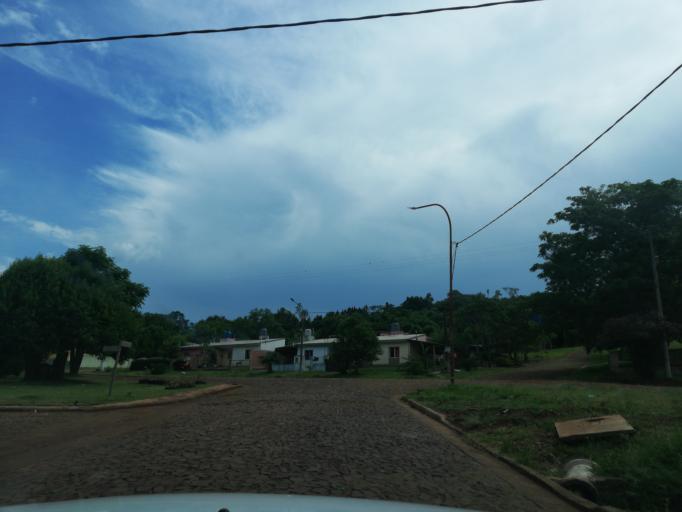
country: AR
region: Misiones
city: Cerro Azul
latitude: -27.5708
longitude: -55.5022
